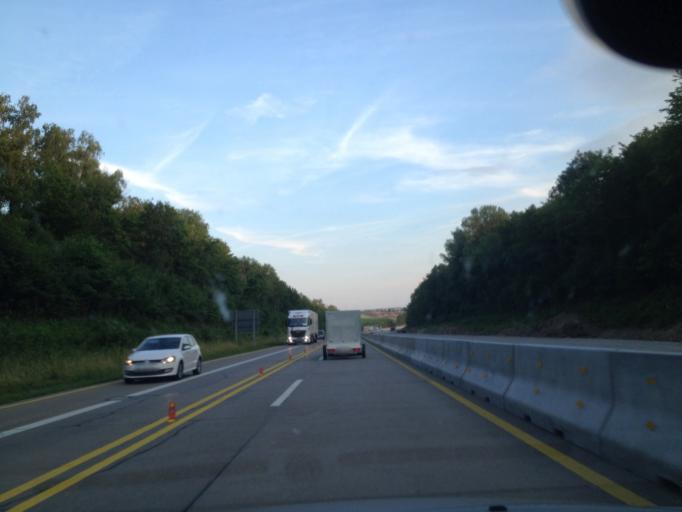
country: DE
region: Bavaria
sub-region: Regierungsbezirk Mittelfranken
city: Gollhofen
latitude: 49.5769
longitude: 10.1721
